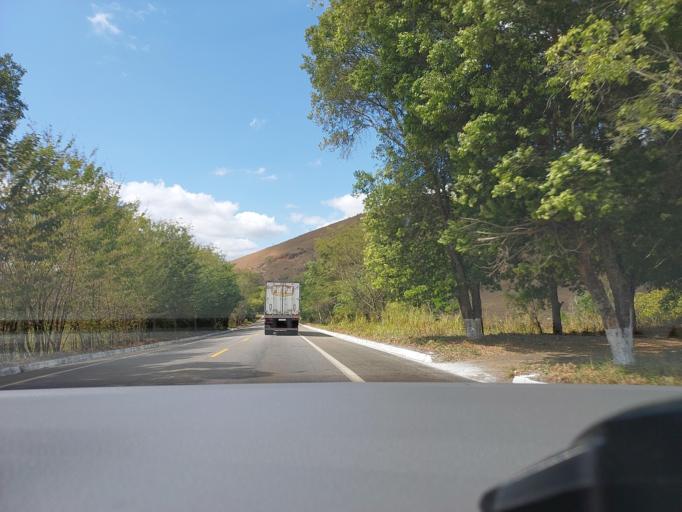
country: BR
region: Minas Gerais
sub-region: Muriae
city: Muriae
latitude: -21.1269
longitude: -42.2393
